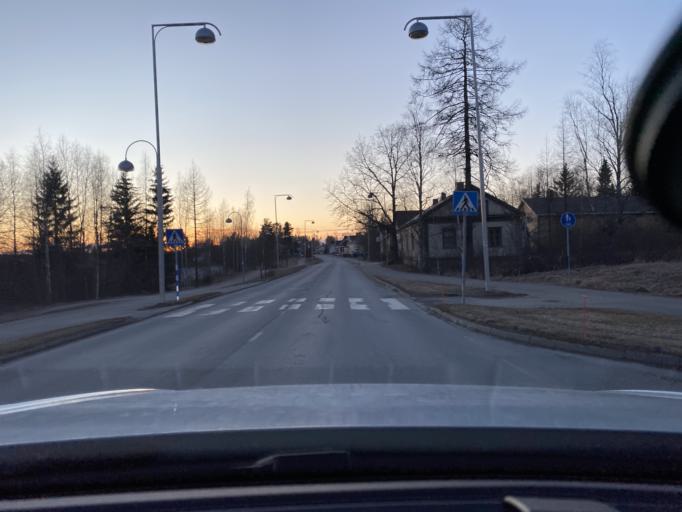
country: FI
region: Pirkanmaa
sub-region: Lounais-Pirkanmaa
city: Punkalaidun
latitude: 61.1082
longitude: 23.1292
